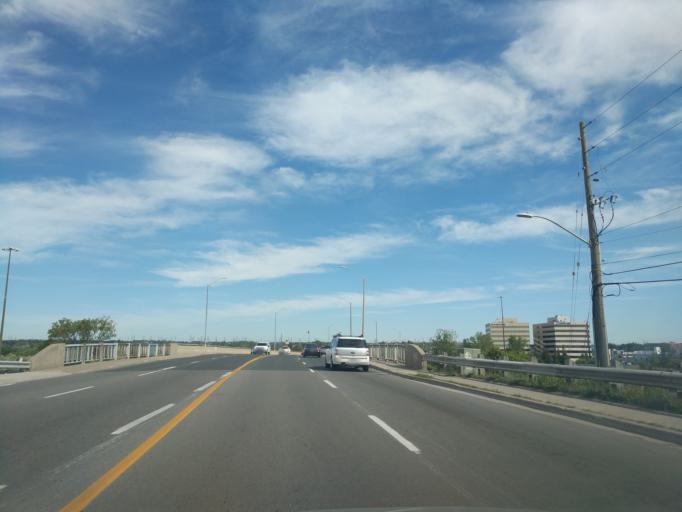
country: CA
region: Ontario
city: Ajax
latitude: 43.8296
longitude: -79.0877
